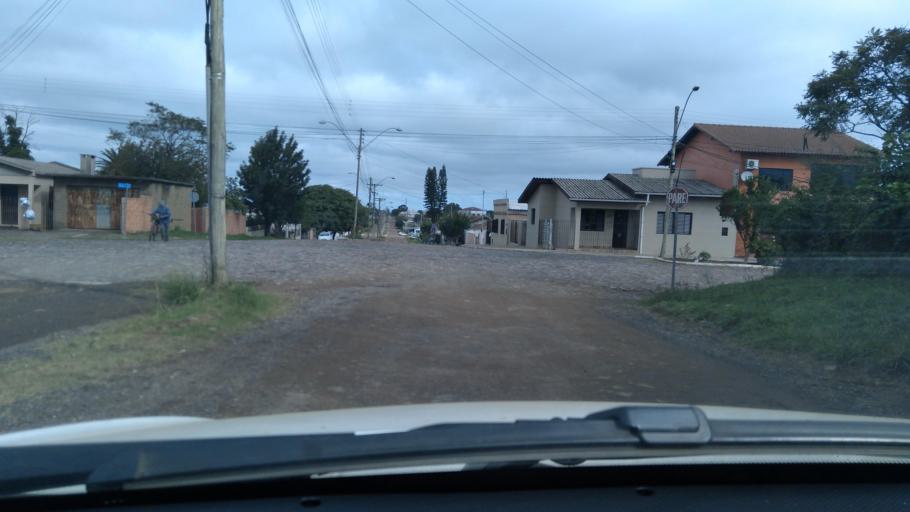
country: BR
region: Rio Grande do Sul
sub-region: Dom Pedrito
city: Dom Pedrito
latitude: -30.9808
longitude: -54.6622
